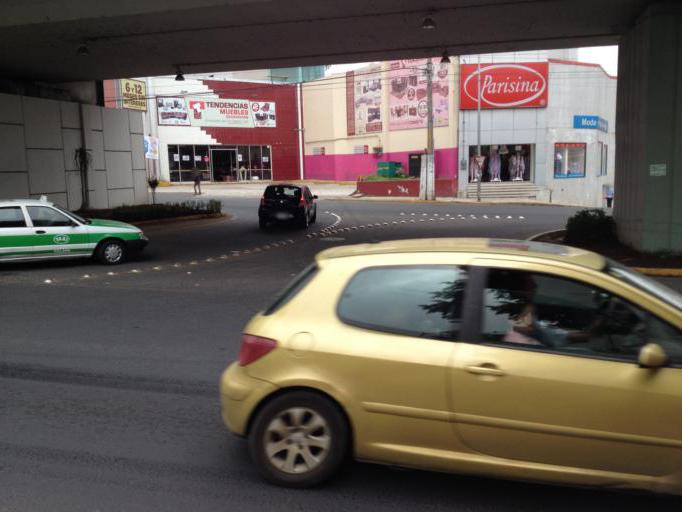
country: MX
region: Veracruz
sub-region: Xalapa
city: Xalapa de Enriquez
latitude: 19.5367
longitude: -96.9081
